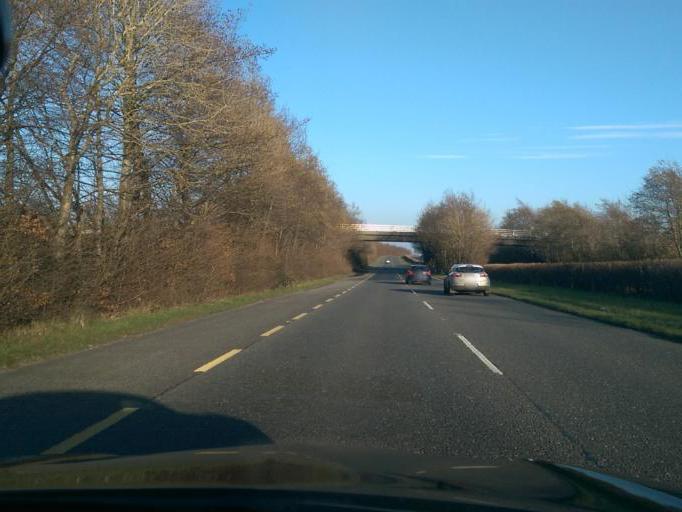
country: IE
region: Connaught
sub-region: County Galway
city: Oranmore
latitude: 53.2785
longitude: -8.9472
